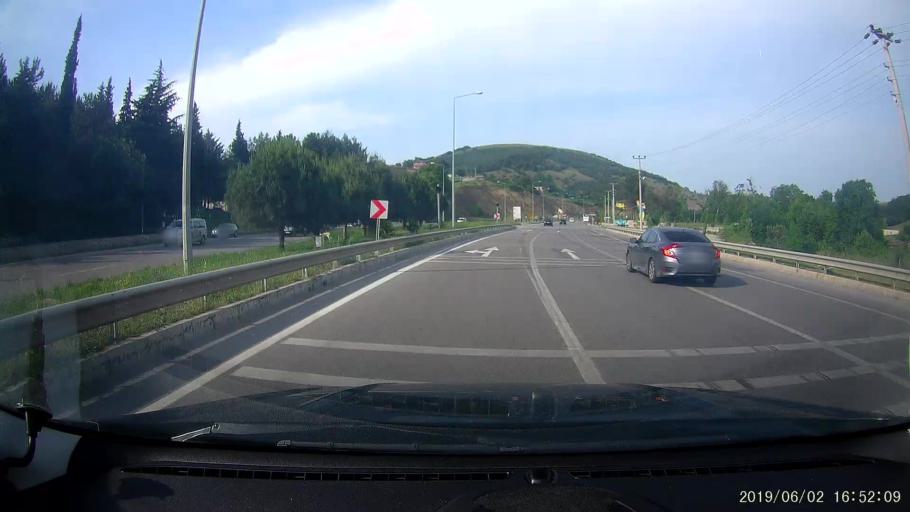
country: TR
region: Samsun
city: Samsun
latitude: 41.2838
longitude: 36.1925
